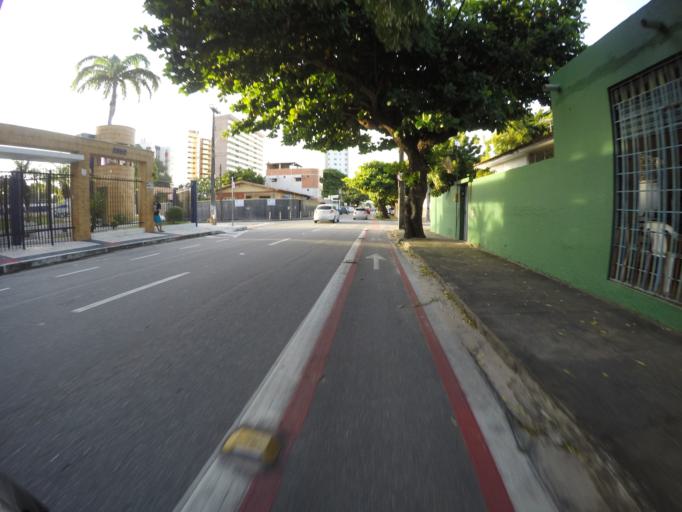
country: BR
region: Ceara
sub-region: Fortaleza
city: Fortaleza
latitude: -3.7469
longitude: -38.5153
